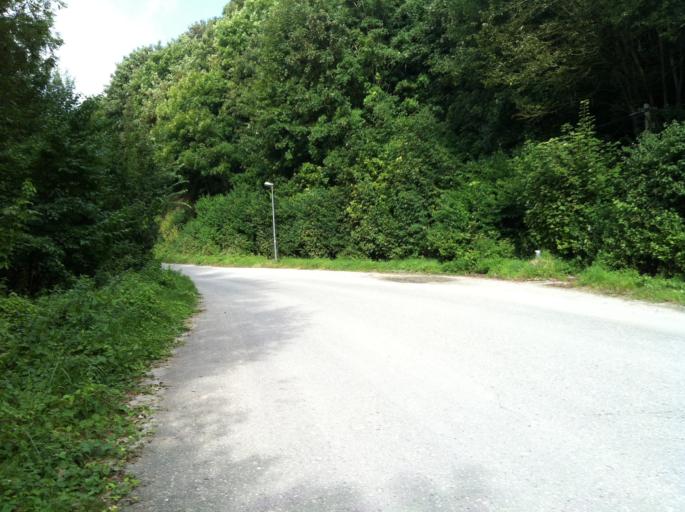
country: DE
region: Bavaria
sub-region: Upper Bavaria
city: Unterfoehring
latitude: 48.2121
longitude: 11.6303
